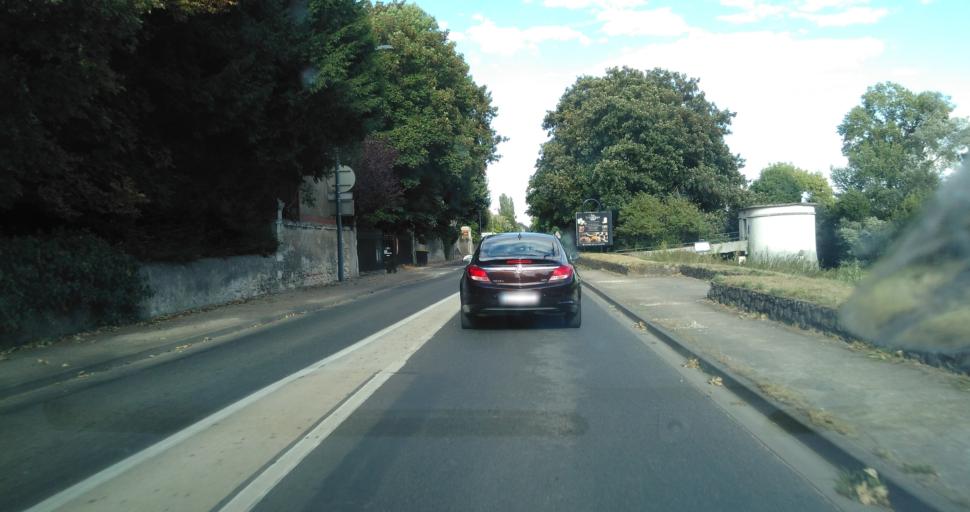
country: FR
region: Centre
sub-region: Departement d'Indre-et-Loire
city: Rochecorbon
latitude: 47.4089
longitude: 0.7602
